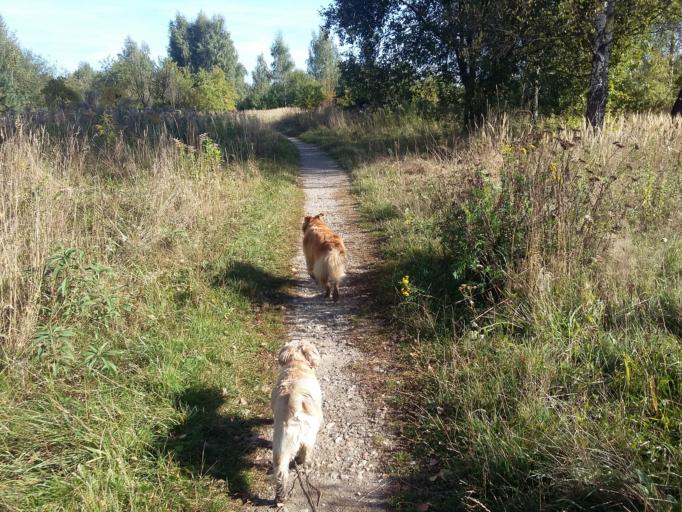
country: PL
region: Lodz Voivodeship
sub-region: Powiat pabianicki
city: Ksawerow
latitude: 51.7307
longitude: 19.3900
